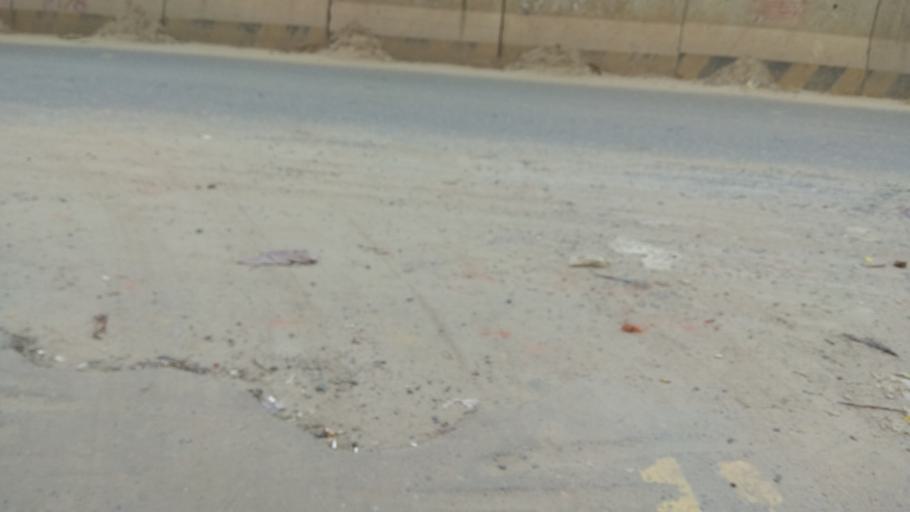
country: BD
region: Dhaka
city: Tungi
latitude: 23.8262
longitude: 90.3644
